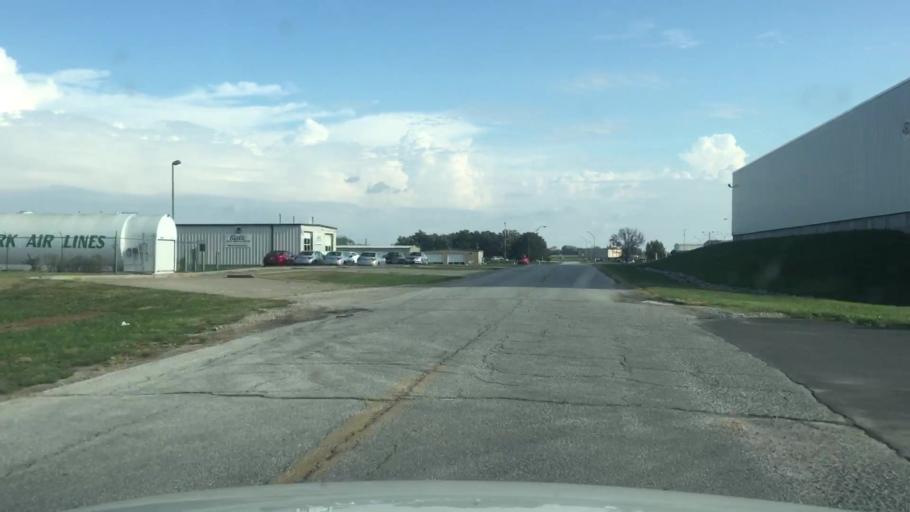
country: US
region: Missouri
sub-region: Boone County
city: Ashland
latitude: 38.8147
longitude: -92.2245
